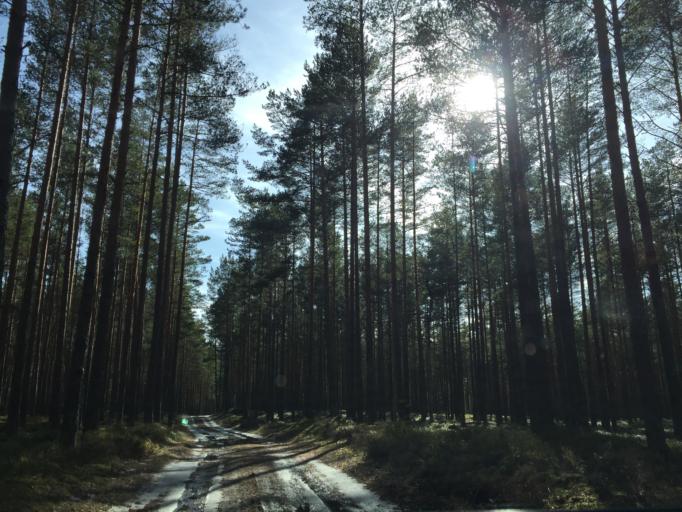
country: EE
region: Paernumaa
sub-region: Paernu linn
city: Parnu
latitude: 58.2336
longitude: 24.5181
